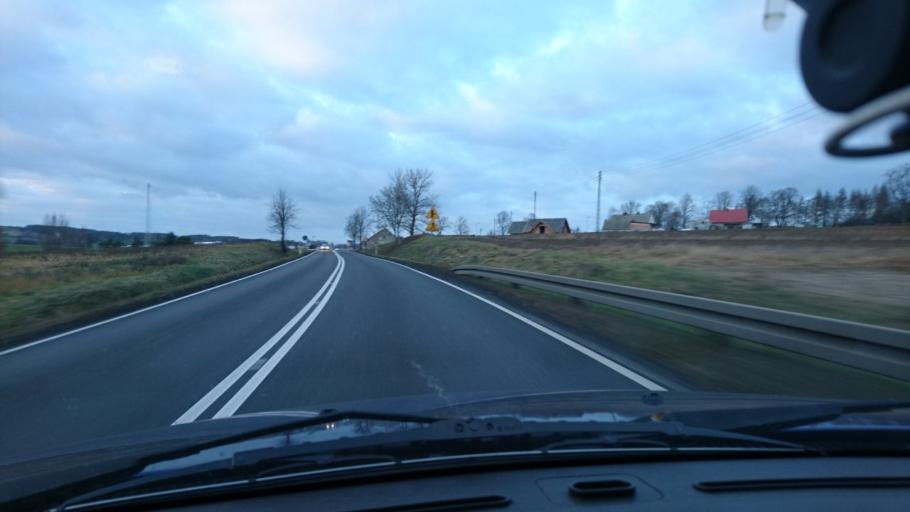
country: PL
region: Greater Poland Voivodeship
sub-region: Powiat ostrzeszowski
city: Ostrzeszow
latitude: 51.3851
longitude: 17.9495
